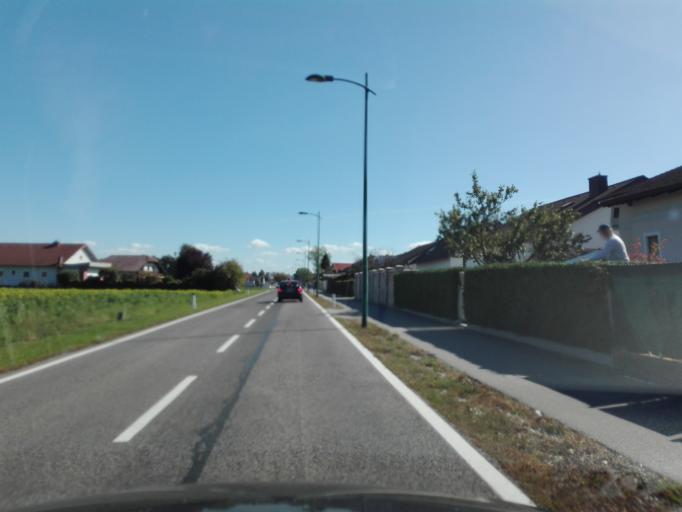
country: AT
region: Lower Austria
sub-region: Politischer Bezirk Amstetten
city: Ennsdorf
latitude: 48.2065
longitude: 14.4998
